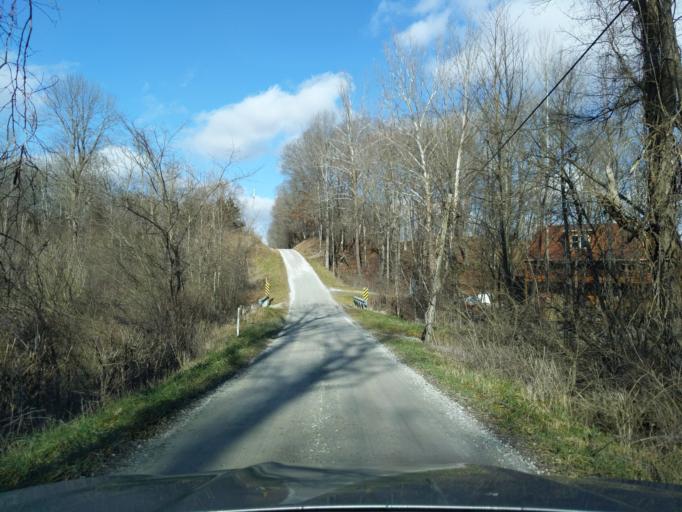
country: US
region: Indiana
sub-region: Decatur County
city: Greensburg
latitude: 39.2508
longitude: -85.4844
